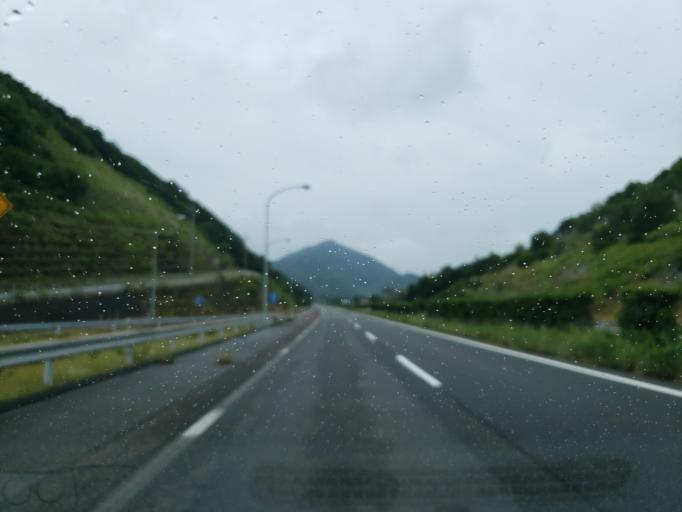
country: JP
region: Tokushima
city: Narutocho-mitsuishi
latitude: 34.2198
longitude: 134.6261
